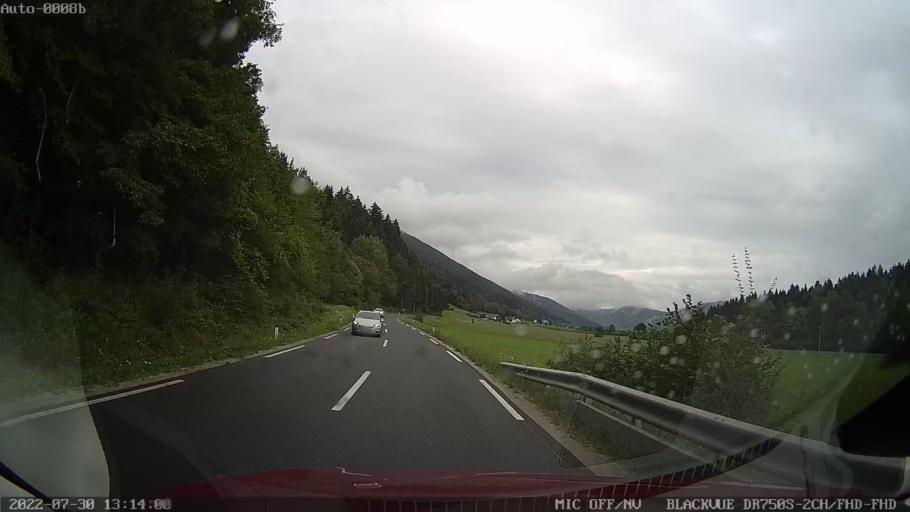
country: SI
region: Dolenjske Toplice
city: Dolenjske Toplice
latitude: 45.7278
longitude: 15.0511
